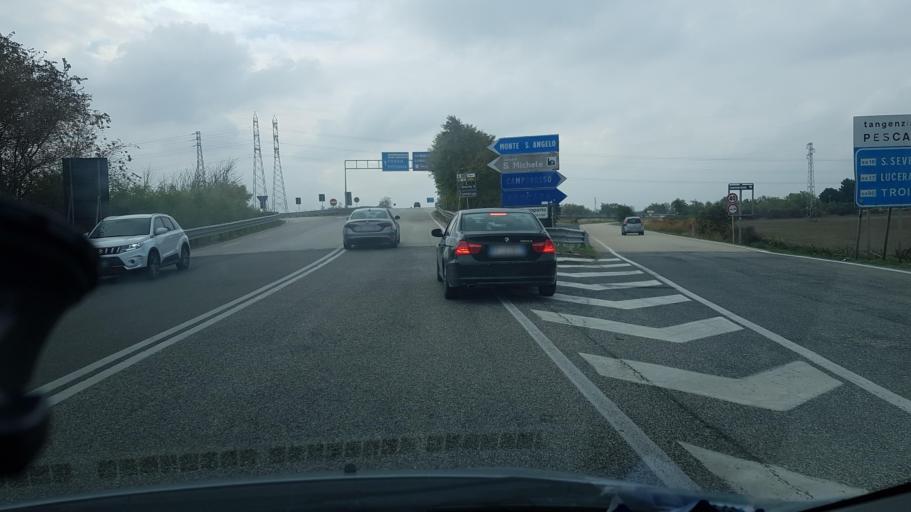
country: IT
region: Apulia
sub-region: Provincia di Foggia
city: Foggia
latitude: 41.4975
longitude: 15.5648
